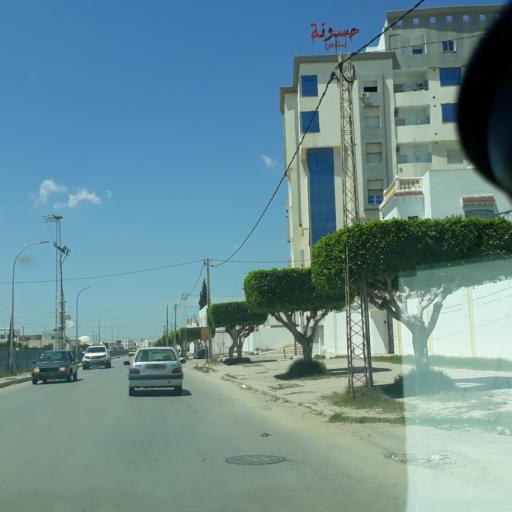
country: TN
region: Safaqis
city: Al Qarmadah
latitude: 34.8055
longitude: 10.7566
